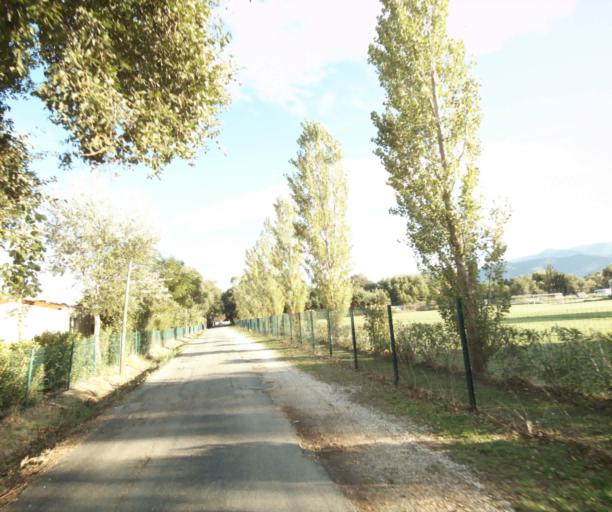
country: FR
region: Languedoc-Roussillon
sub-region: Departement des Pyrenees-Orientales
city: Argelers
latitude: 42.5685
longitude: 3.0121
